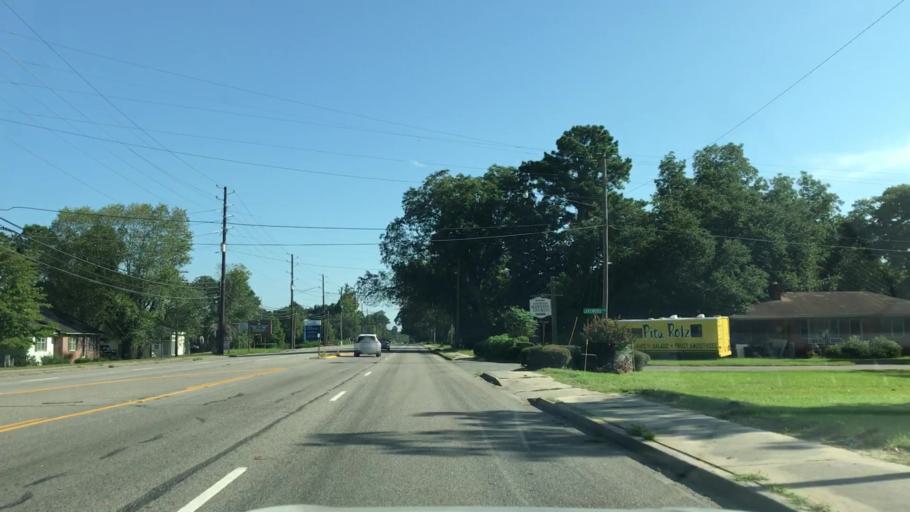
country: US
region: South Carolina
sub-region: Georgetown County
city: Georgetown
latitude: 33.4065
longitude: -79.2873
